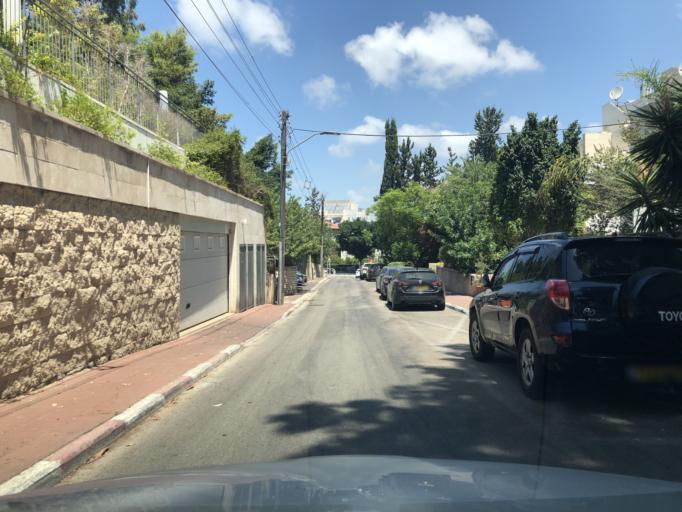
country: IL
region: Tel Aviv
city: Ramat Gan
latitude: 32.0855
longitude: 34.8085
